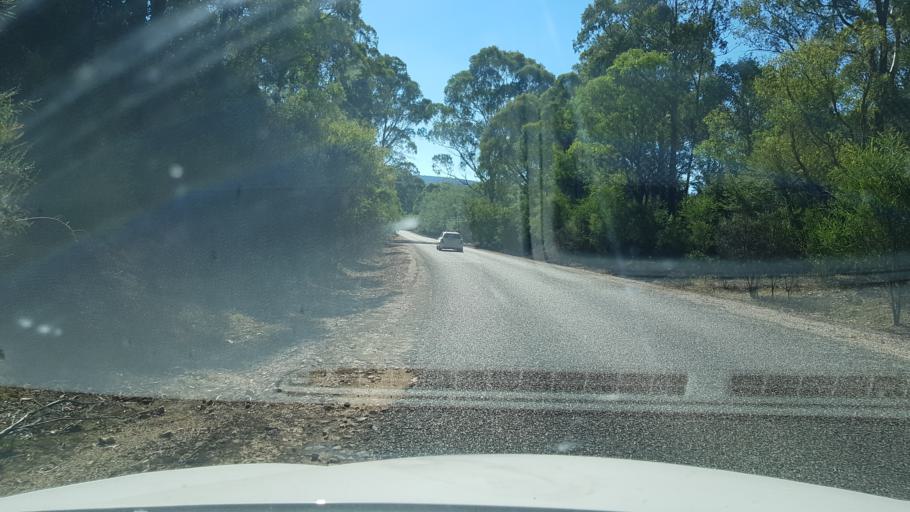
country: AU
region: Victoria
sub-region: Mansfield
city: Mansfield
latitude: -36.8968
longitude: 146.3866
